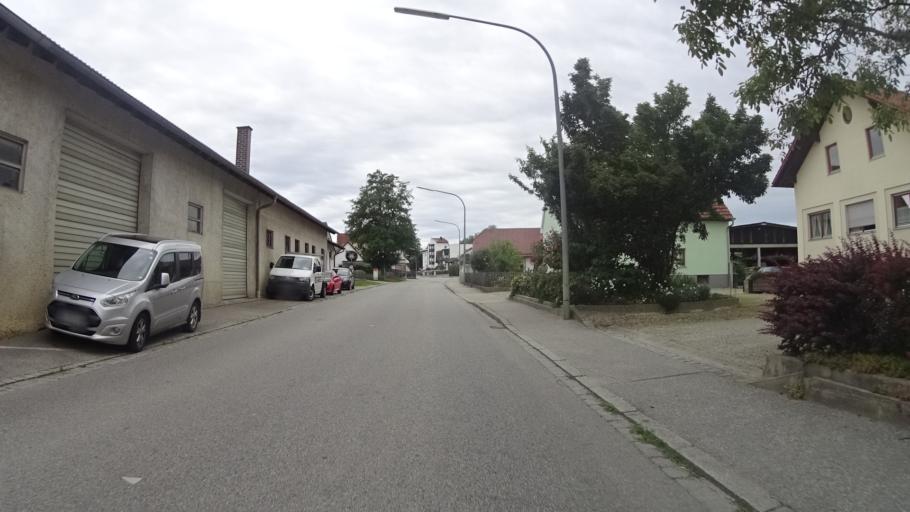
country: DE
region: Bavaria
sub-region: Lower Bavaria
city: Velden
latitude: 48.3677
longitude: 12.2519
